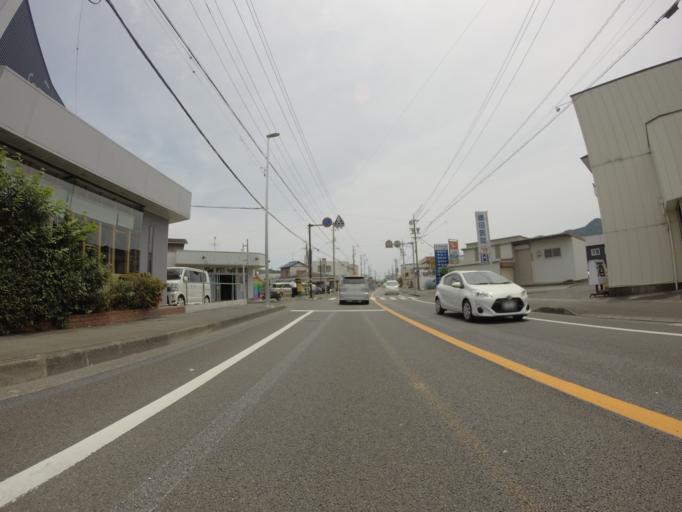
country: JP
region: Shizuoka
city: Shizuoka-shi
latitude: 34.9835
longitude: 138.3347
